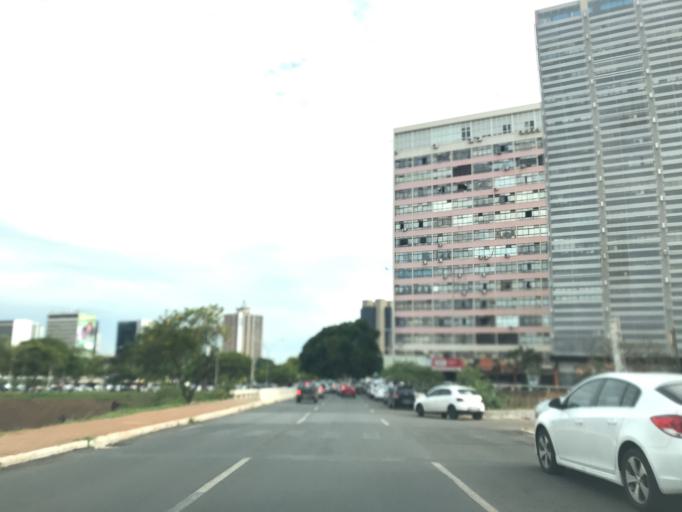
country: BR
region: Federal District
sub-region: Brasilia
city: Brasilia
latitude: -15.7961
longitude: -47.8859
